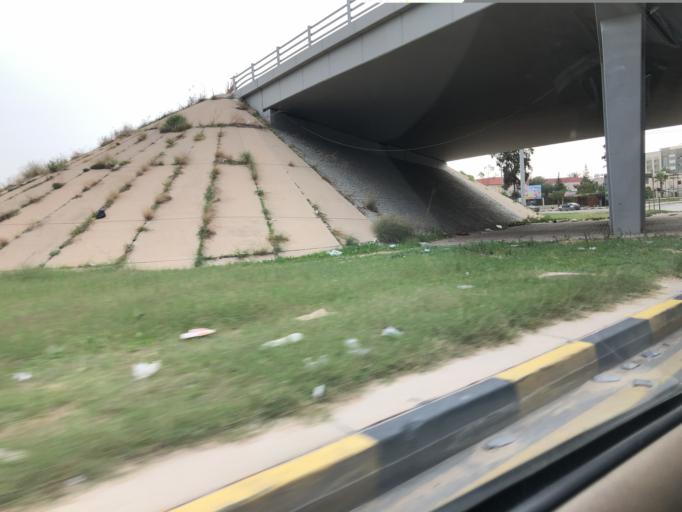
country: LY
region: Tripoli
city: Tripoli
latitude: 32.8676
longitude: 13.1361
